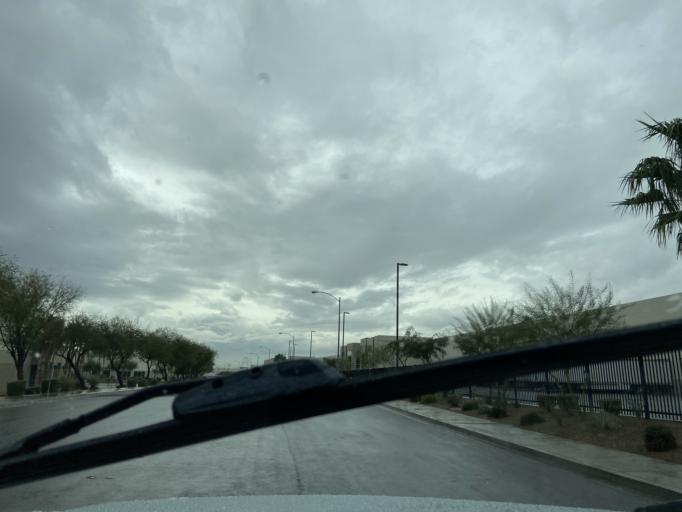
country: US
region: Nevada
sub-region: Clark County
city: Sunrise Manor
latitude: 36.2374
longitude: -115.1021
